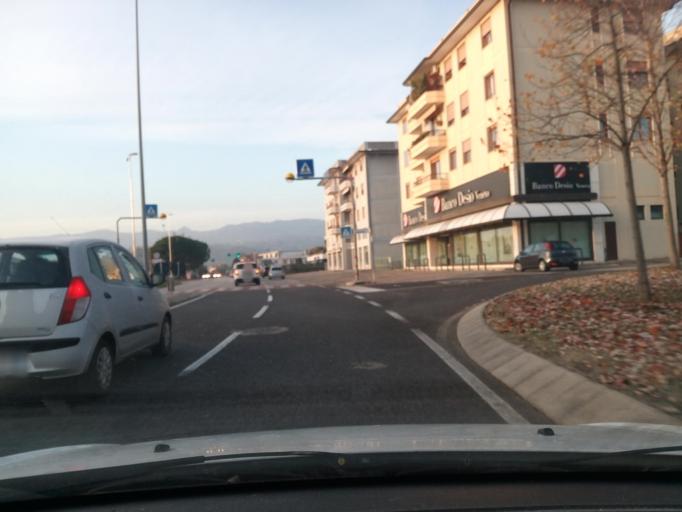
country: IT
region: Veneto
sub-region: Provincia di Vicenza
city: Schio
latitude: 45.7147
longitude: 11.3768
